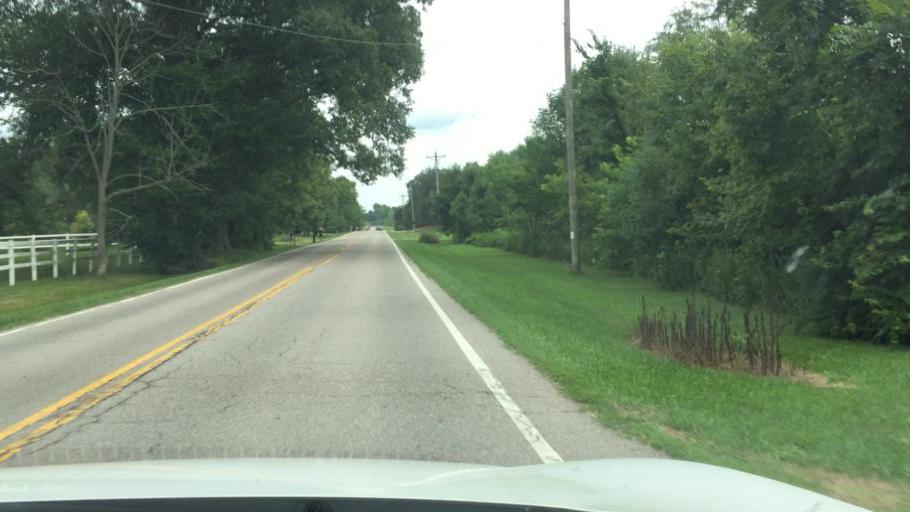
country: US
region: Ohio
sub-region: Union County
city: Marysville
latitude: 40.2300
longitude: -83.4619
